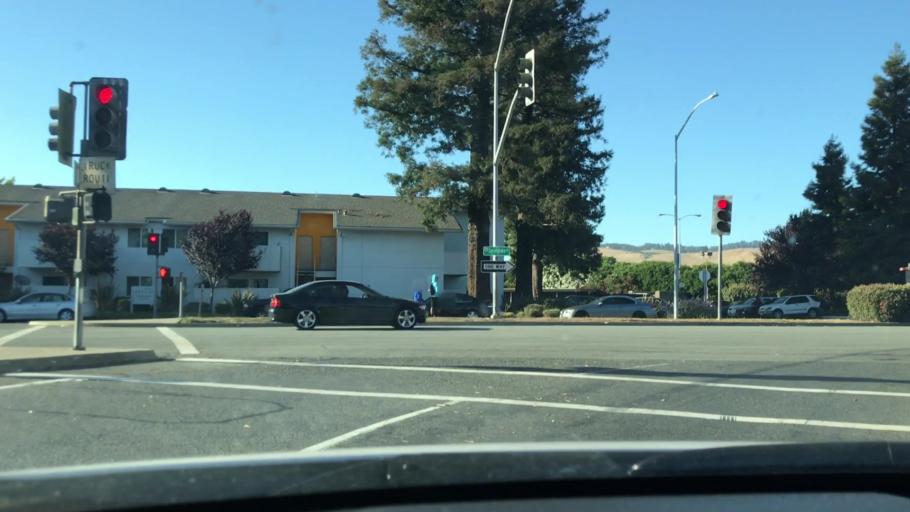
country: US
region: California
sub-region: Alameda County
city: San Lorenzo
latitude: 37.6922
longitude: -122.1313
